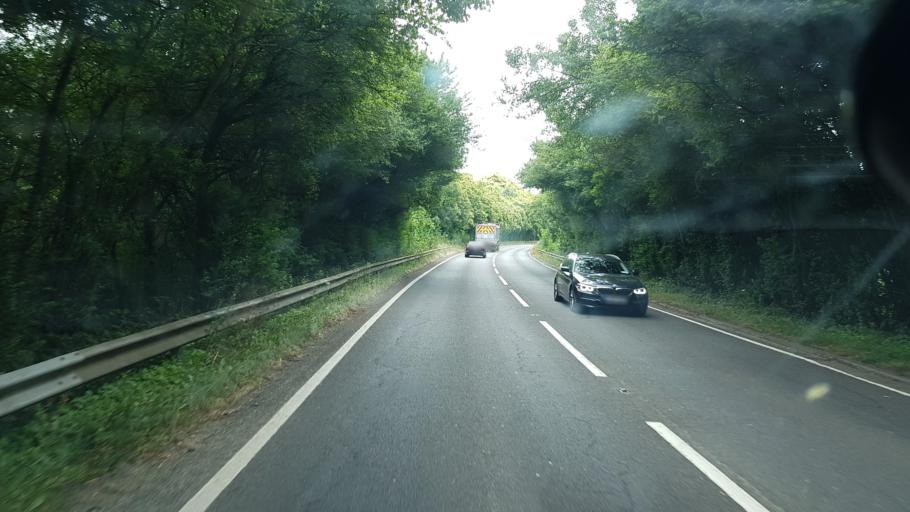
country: GB
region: England
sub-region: Surrey
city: Godstone
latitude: 51.2434
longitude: -0.0484
